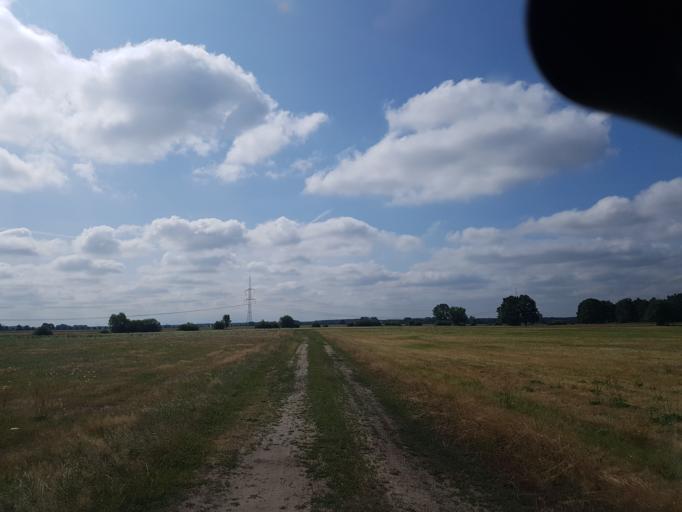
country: DE
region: Brandenburg
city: Schonborn
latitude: 51.5844
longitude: 13.5144
